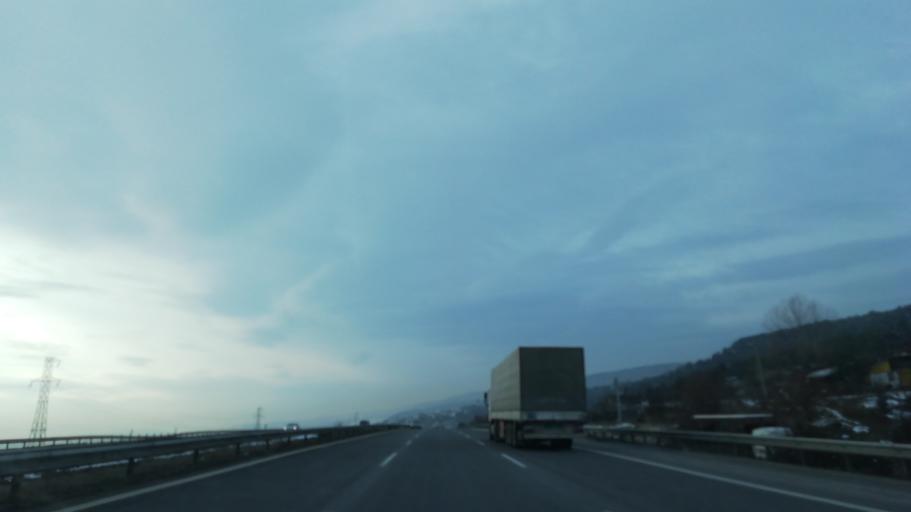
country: TR
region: Bolu
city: Bolu
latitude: 40.7640
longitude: 31.6142
